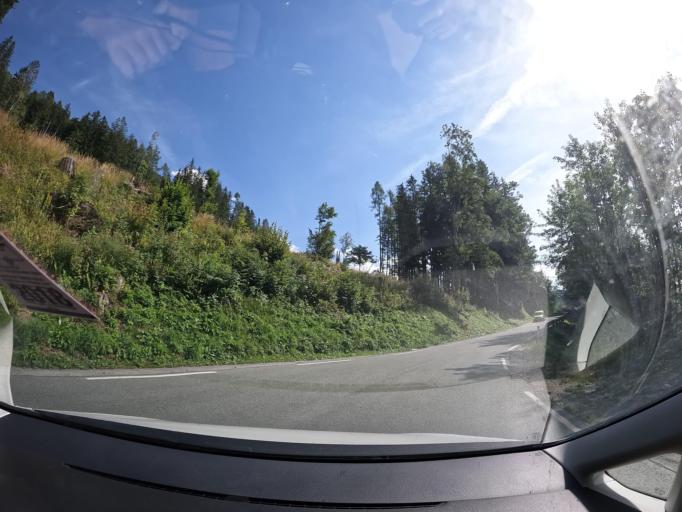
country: AT
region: Carinthia
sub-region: Politischer Bezirk Sankt Veit an der Glan
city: Liebenfels
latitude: 46.7100
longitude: 14.2669
